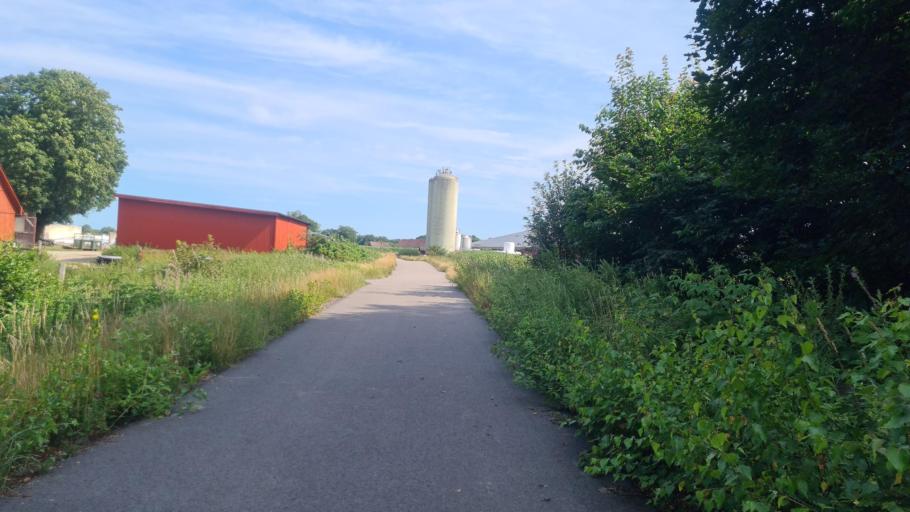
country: SE
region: Kronoberg
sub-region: Ljungby Kommun
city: Lagan
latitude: 56.8721
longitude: 13.9815
